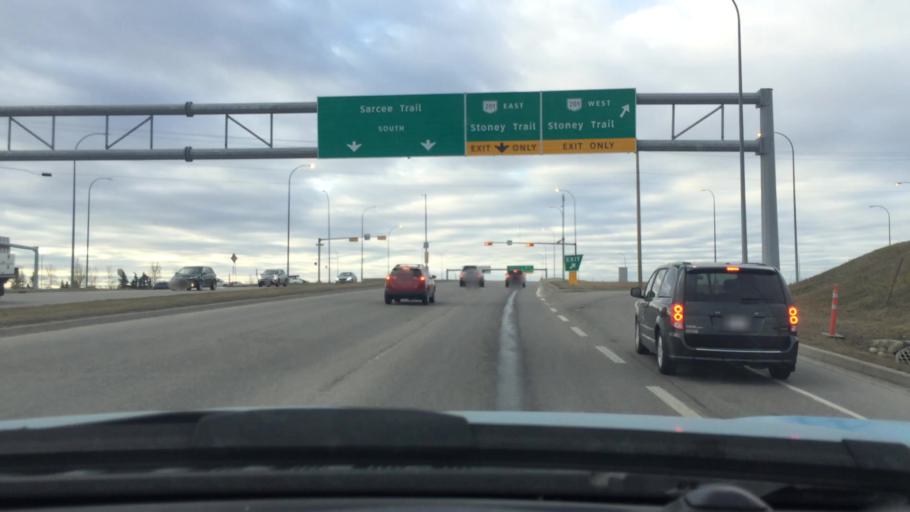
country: CA
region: Alberta
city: Calgary
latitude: 51.1543
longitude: -114.1641
